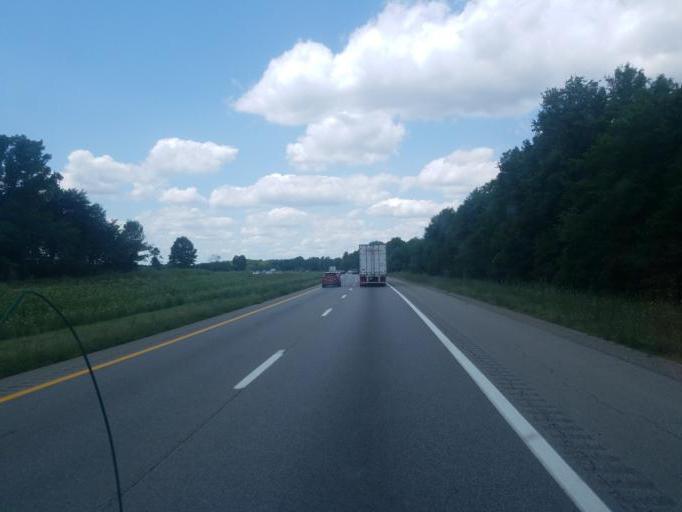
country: US
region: Ohio
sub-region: Licking County
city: Etna
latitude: 39.9521
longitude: -82.7412
